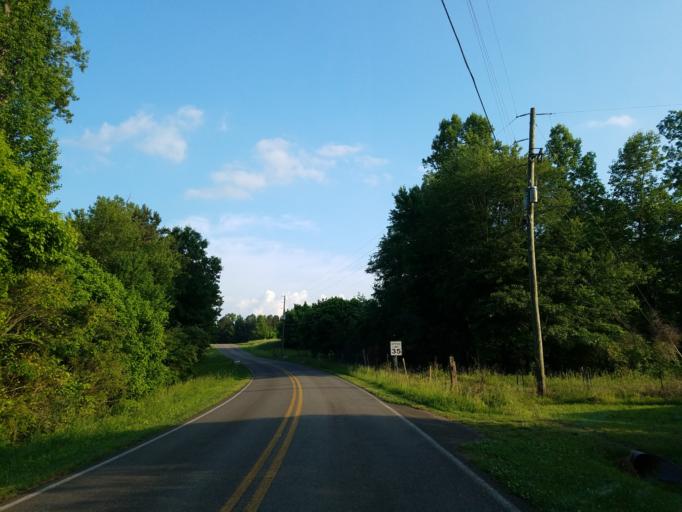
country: US
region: Georgia
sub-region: Cherokee County
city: Ball Ground
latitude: 34.3149
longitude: -84.3708
